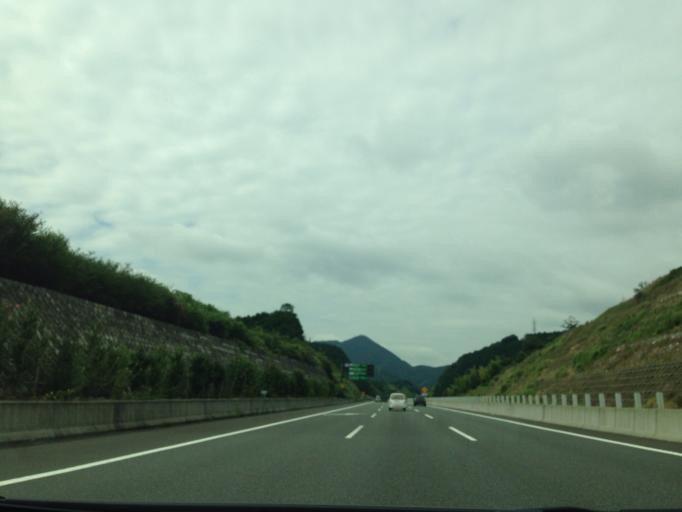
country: JP
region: Shizuoka
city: Shizuoka-shi
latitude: 35.0327
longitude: 138.3623
